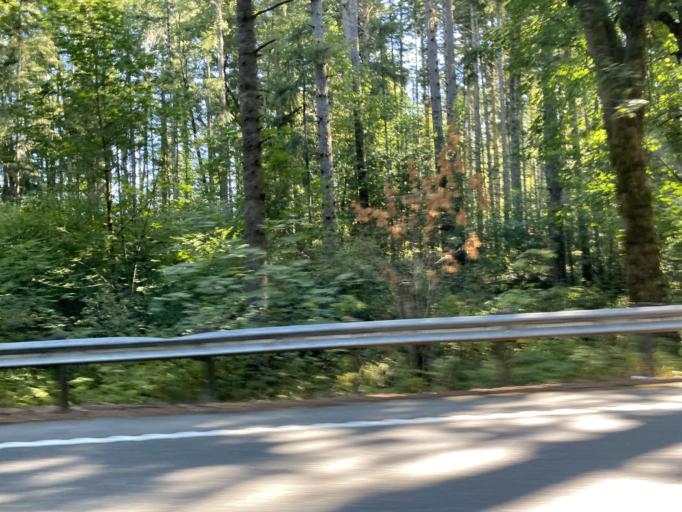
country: US
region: Washington
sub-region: Thurston County
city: Rainier
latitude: 46.9342
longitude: -122.7587
